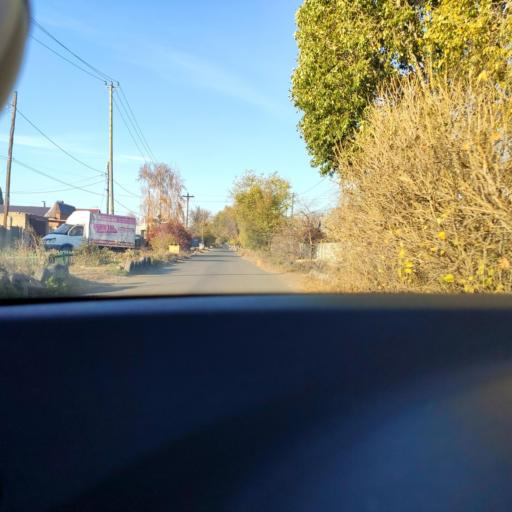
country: RU
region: Samara
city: Petra-Dubrava
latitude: 53.2471
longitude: 50.3281
